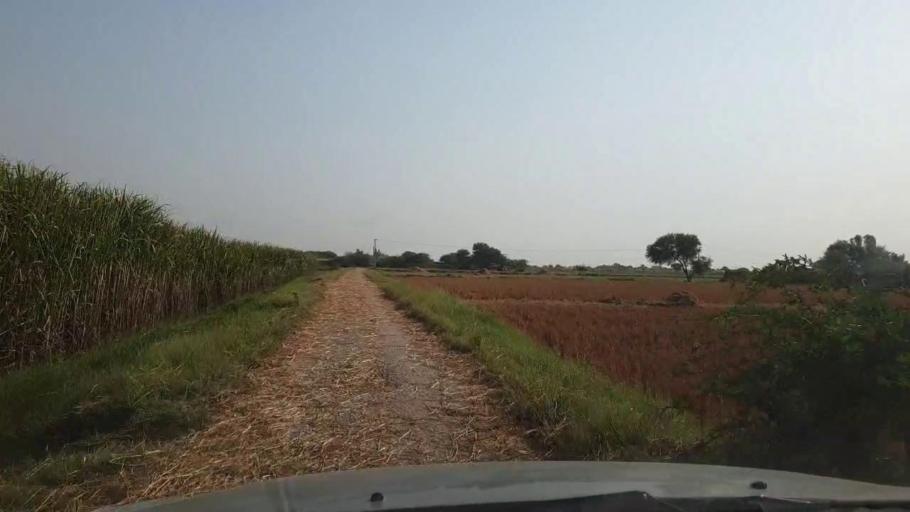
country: PK
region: Sindh
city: Bulri
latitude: 24.9170
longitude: 68.3131
